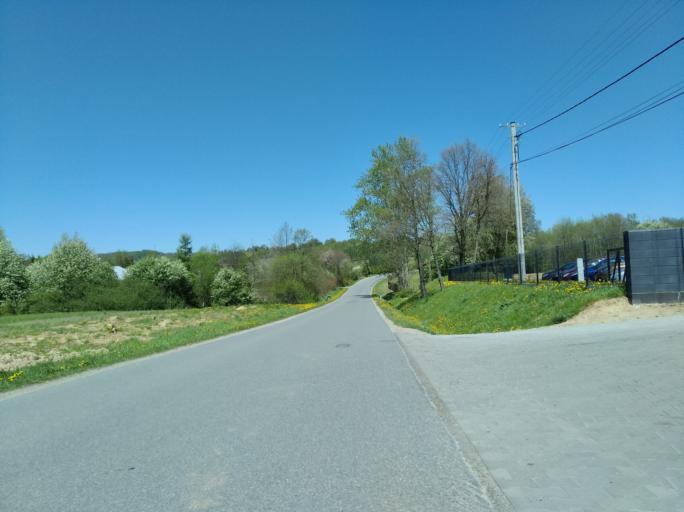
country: PL
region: Subcarpathian Voivodeship
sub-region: Powiat debicki
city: Brzostek
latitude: 49.8872
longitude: 21.4052
